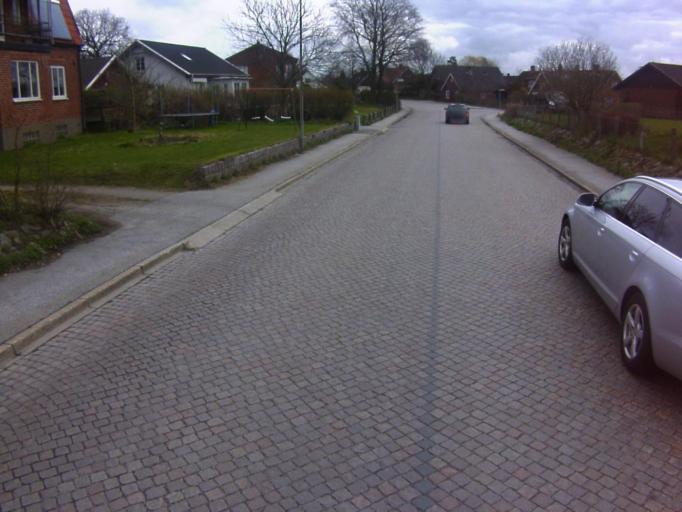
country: SE
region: Skane
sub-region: Lunds Kommun
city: Lund
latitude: 55.7930
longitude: 13.2038
